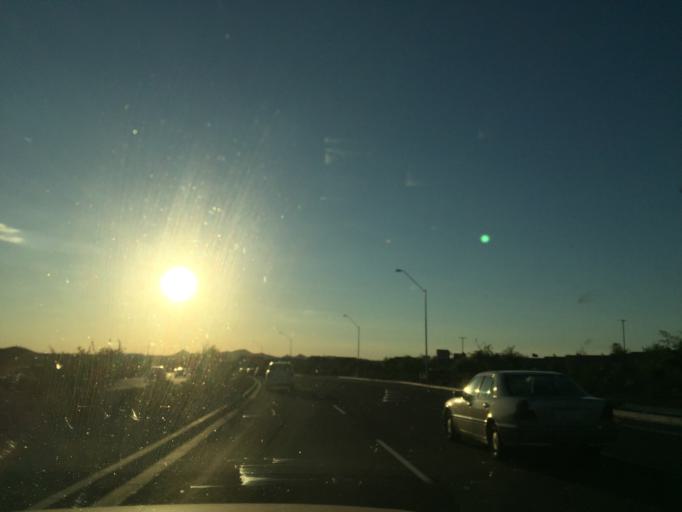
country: US
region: Arizona
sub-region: Maricopa County
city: Sun City West
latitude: 33.7132
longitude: -112.2795
